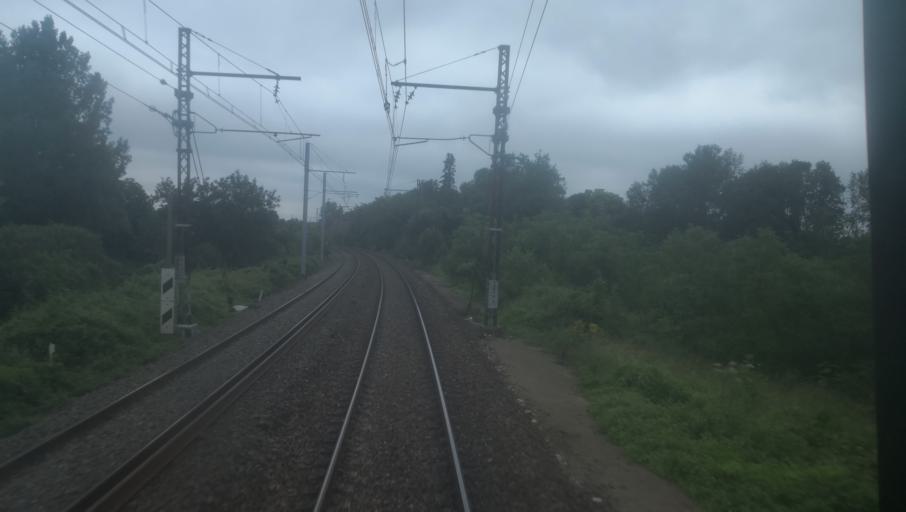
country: FR
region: Centre
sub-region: Departement de l'Indre
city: Sainte-Lizaigne
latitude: 47.0228
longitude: 2.0410
